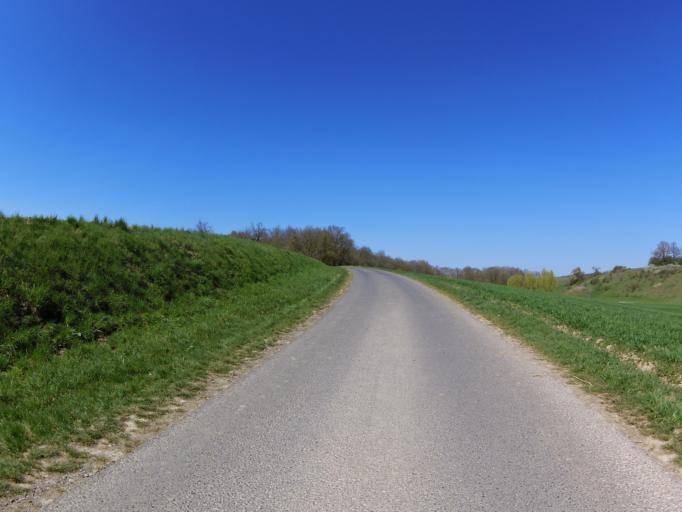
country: DE
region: Bavaria
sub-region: Regierungsbezirk Unterfranken
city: Rottendorf
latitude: 49.8223
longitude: 10.0505
